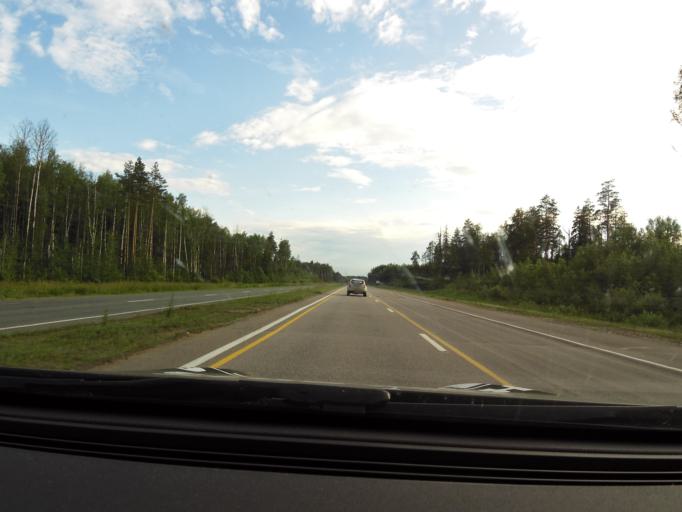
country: RU
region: Vladimir
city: Kameshkovo
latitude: 56.1598
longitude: 40.9276
